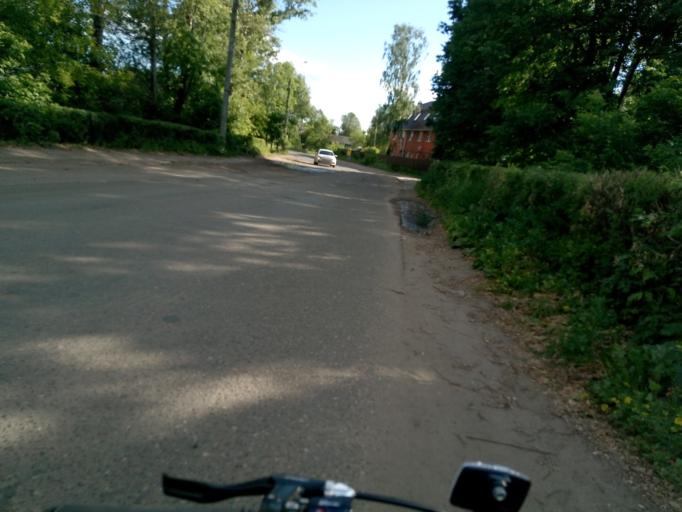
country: RU
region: Jaroslavl
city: Yaroslavl
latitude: 57.6407
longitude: 39.9131
